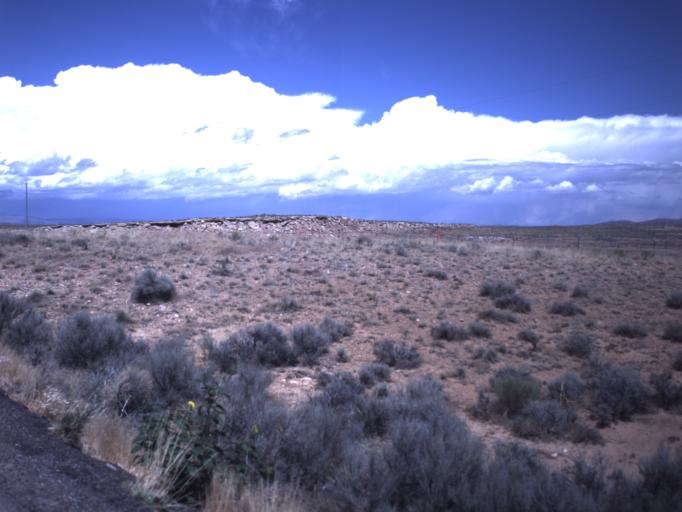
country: US
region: Utah
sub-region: Uintah County
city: Maeser
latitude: 40.2832
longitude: -109.6830
